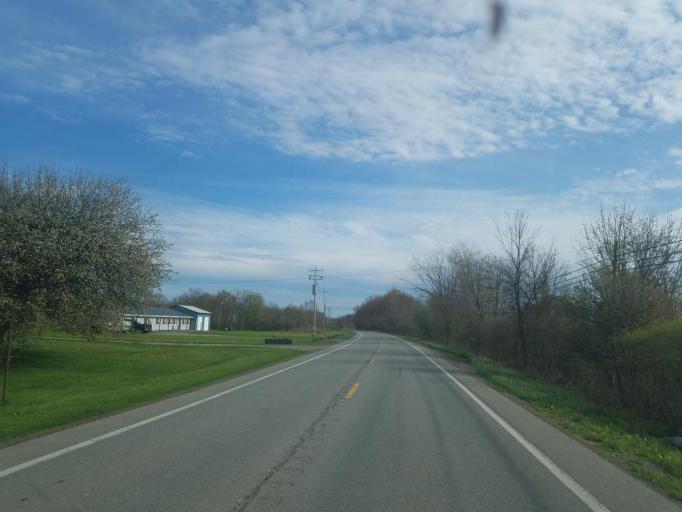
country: US
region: Pennsylvania
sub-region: Mercer County
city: Stoneboro
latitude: 41.3973
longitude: -80.0736
